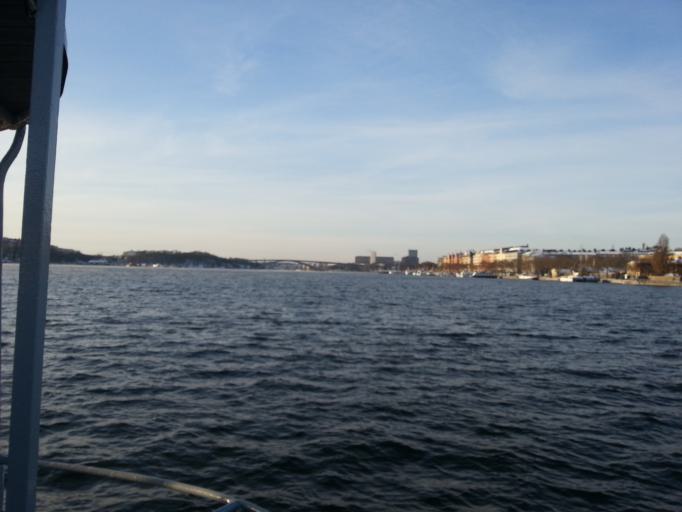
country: SE
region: Stockholm
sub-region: Stockholms Kommun
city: Stockholm
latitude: 59.3255
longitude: 18.0581
